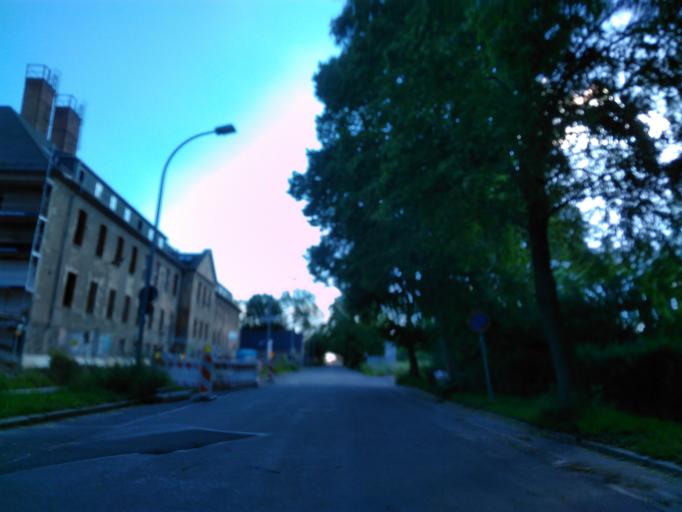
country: DE
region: Thuringia
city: Weimar
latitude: 50.9906
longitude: 11.3466
